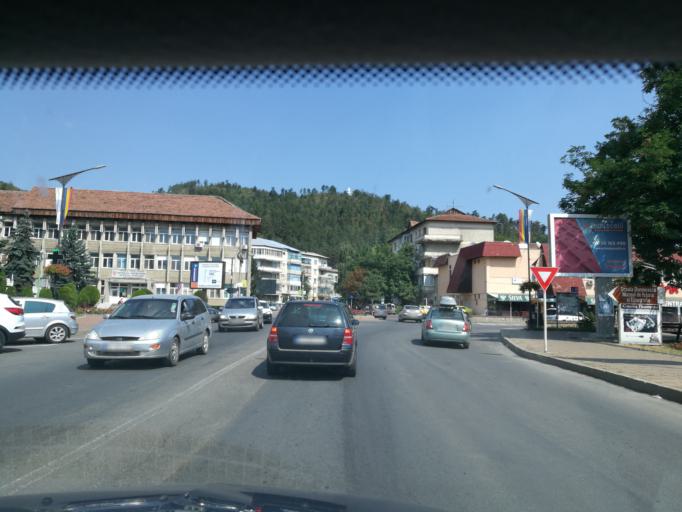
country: RO
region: Neamt
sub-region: Oras Targu Neamt
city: Targu Neamt
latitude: 47.2063
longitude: 26.3599
